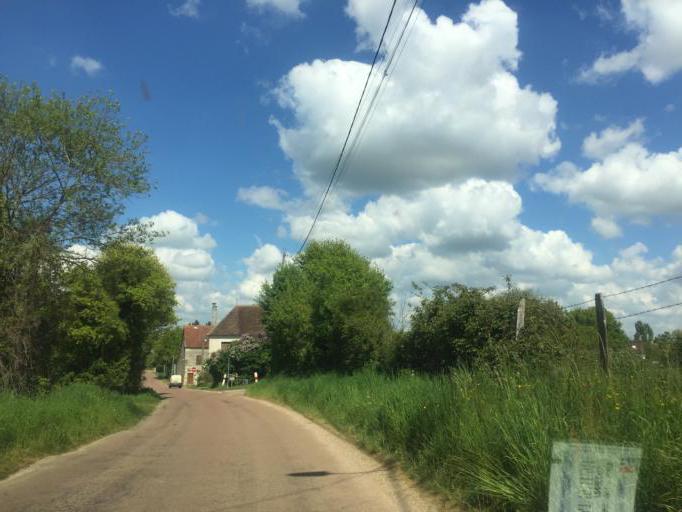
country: FR
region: Bourgogne
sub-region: Departement de l'Yonne
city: Fontenailles
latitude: 47.4930
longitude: 3.3734
